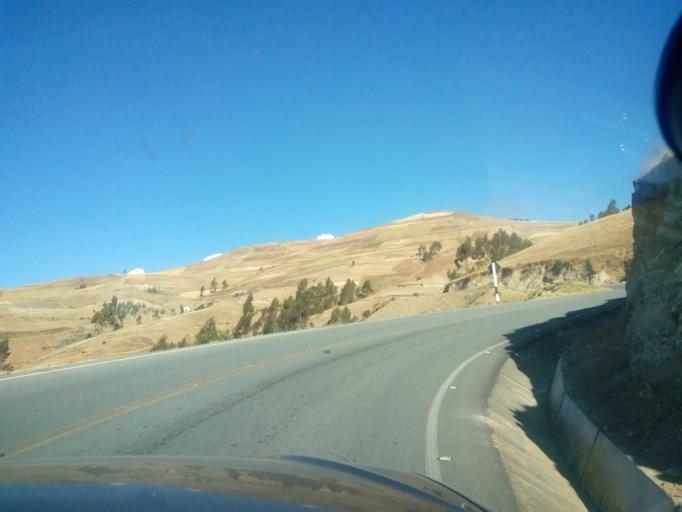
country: PE
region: Apurimac
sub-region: Provincia de Andahuaylas
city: Pacucha
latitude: -13.6578
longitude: -73.2893
